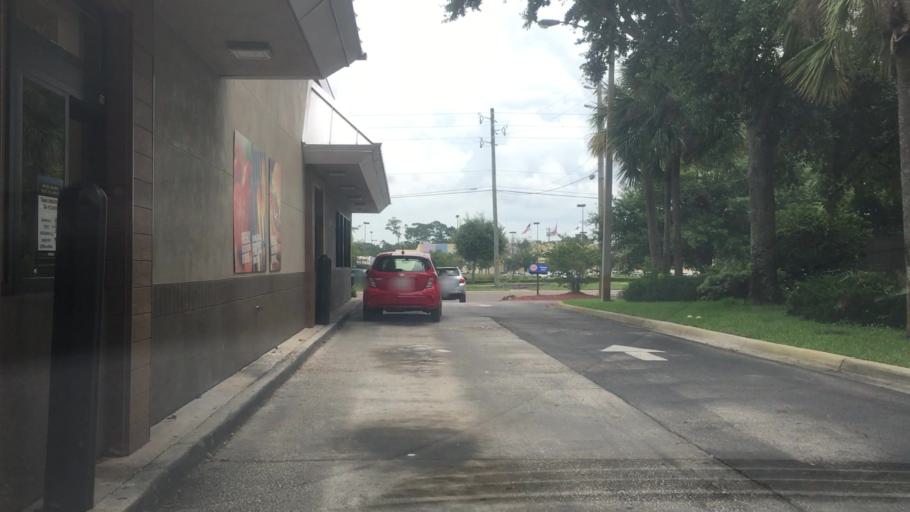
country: US
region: Florida
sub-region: Duval County
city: Jacksonville
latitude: 30.3253
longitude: -81.5476
